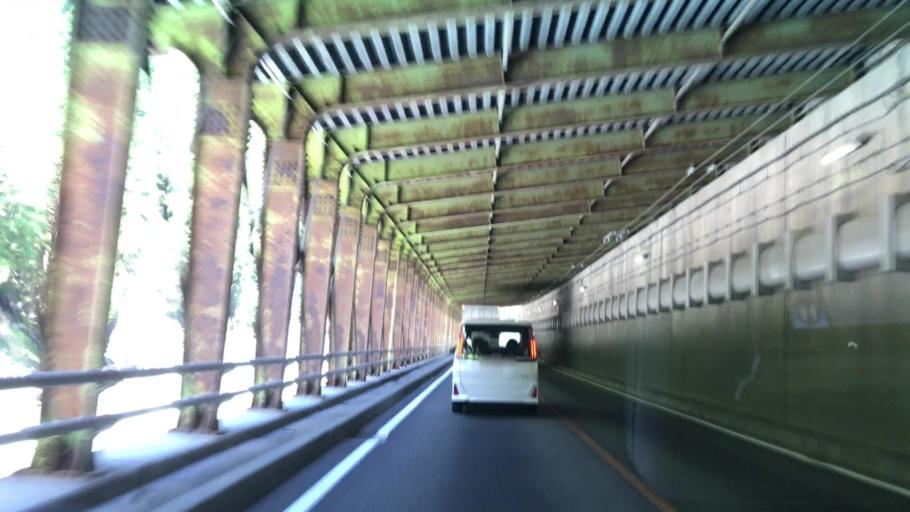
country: JP
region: Hokkaido
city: Shimo-furano
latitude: 42.9435
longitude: 142.5990
